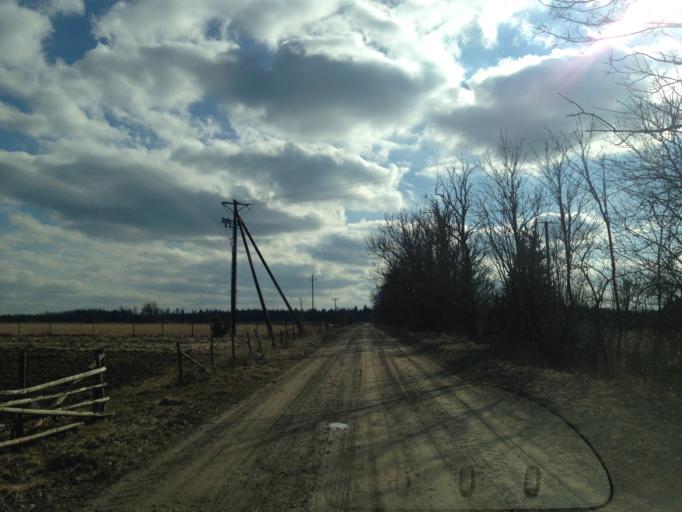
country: EE
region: Harju
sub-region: Nissi vald
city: Riisipere
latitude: 59.1366
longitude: 24.4327
